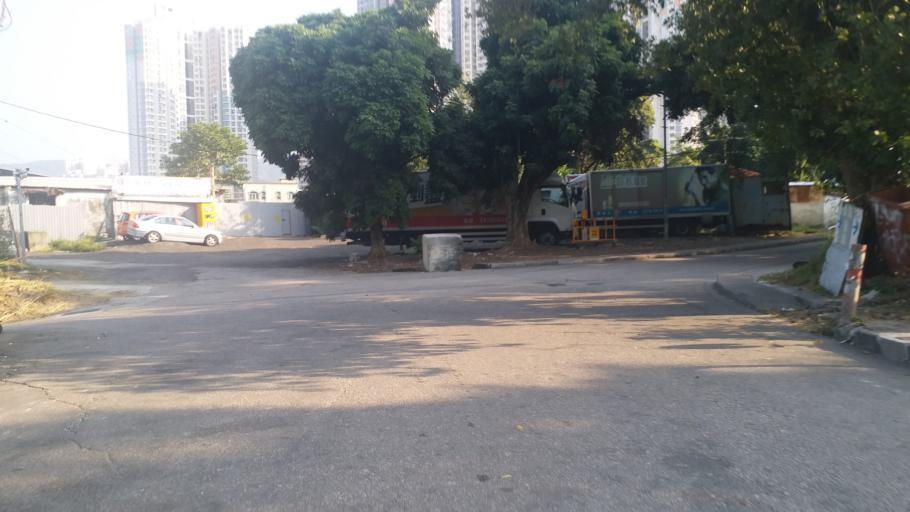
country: HK
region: Tuen Mun
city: Tuen Mun
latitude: 22.4172
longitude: 113.9737
